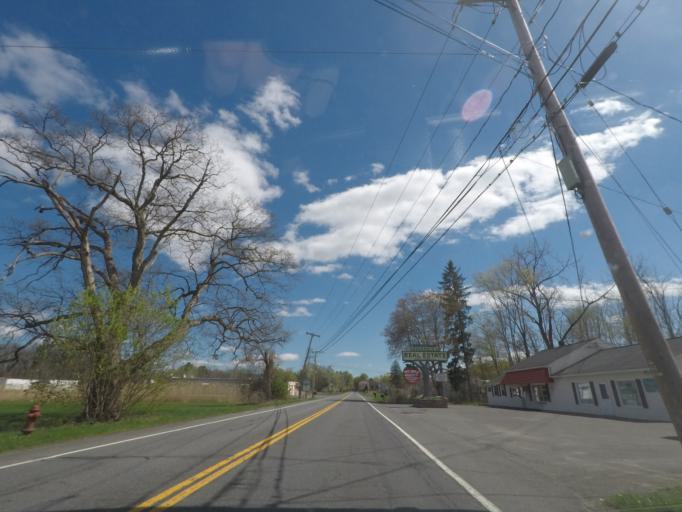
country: US
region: New York
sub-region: Columbia County
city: Oakdale
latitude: 42.2308
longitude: -73.7512
